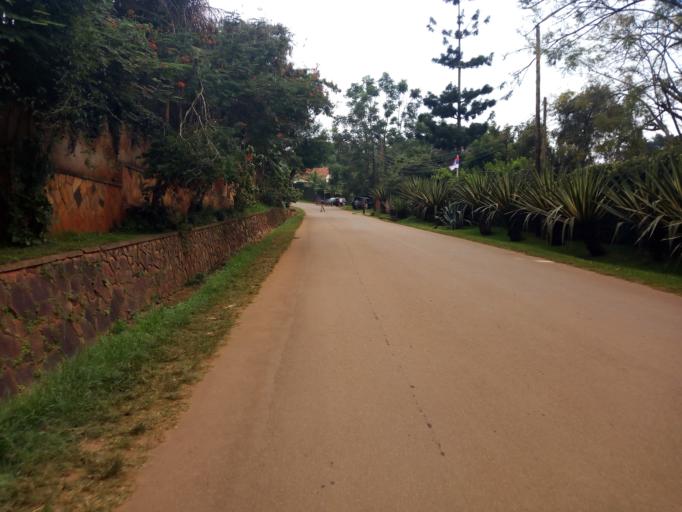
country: UG
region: Central Region
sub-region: Wakiso District
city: Kireka
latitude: 0.3256
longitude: 32.6251
